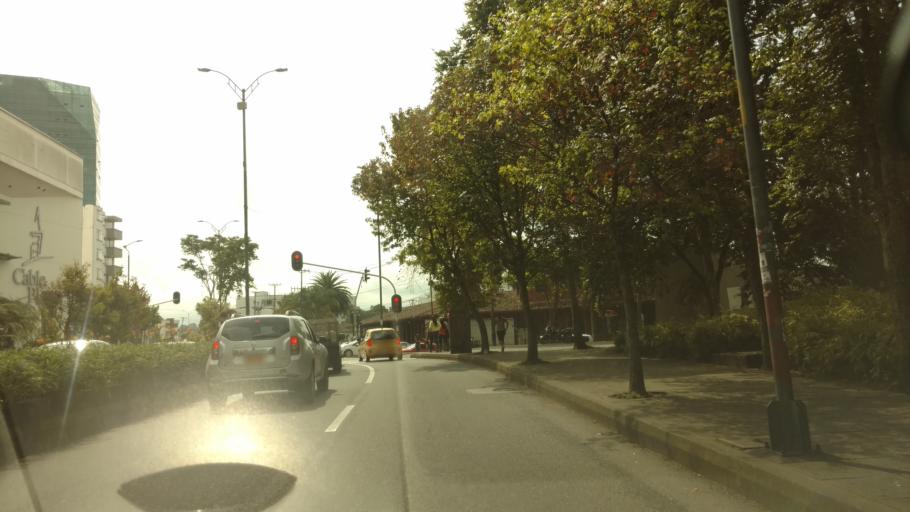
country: CO
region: Caldas
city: Villamaria
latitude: 5.0565
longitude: -75.4863
